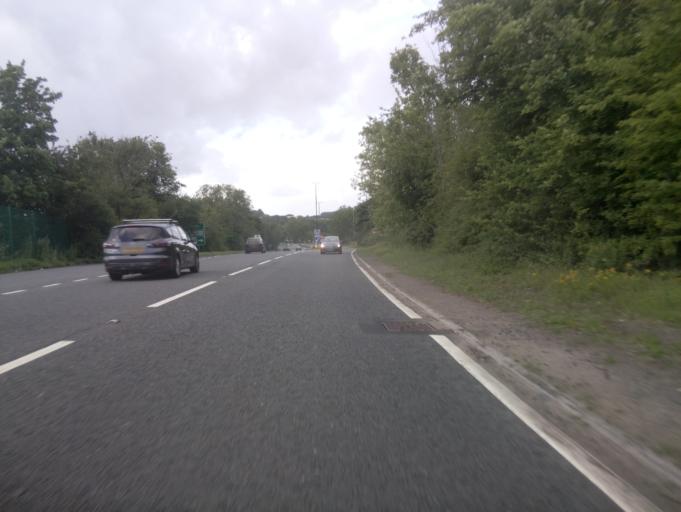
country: GB
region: England
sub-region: Gloucestershire
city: Shipton Village
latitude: 51.8737
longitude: -1.9644
